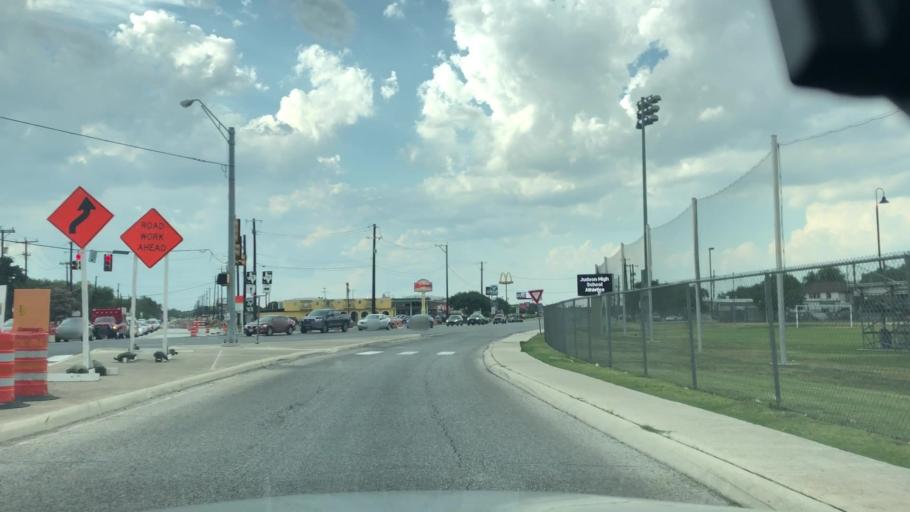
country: US
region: Texas
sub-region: Bexar County
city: Converse
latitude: 29.5092
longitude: -98.3080
